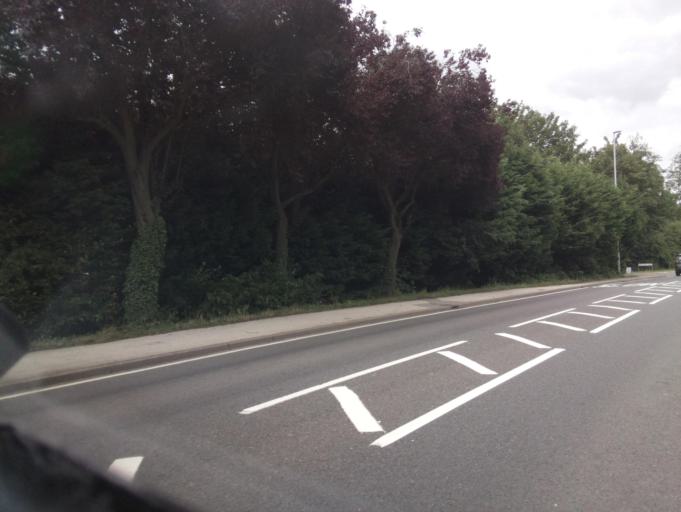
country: GB
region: England
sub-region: Nottinghamshire
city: Burton Joyce
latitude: 52.9922
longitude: -1.0285
